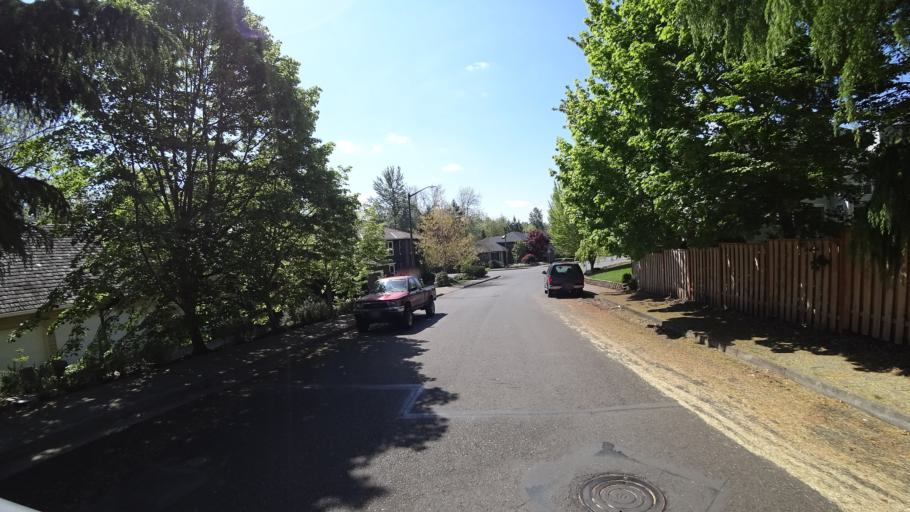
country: US
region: Oregon
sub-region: Washington County
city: King City
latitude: 45.4311
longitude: -122.8375
